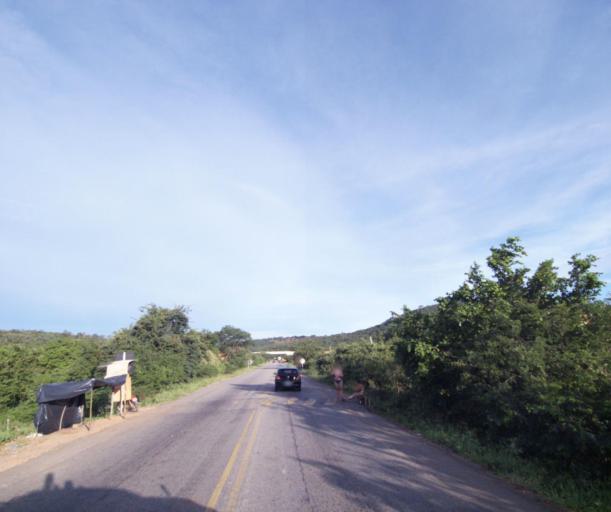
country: BR
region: Bahia
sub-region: Caetite
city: Caetite
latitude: -14.1710
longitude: -42.2248
